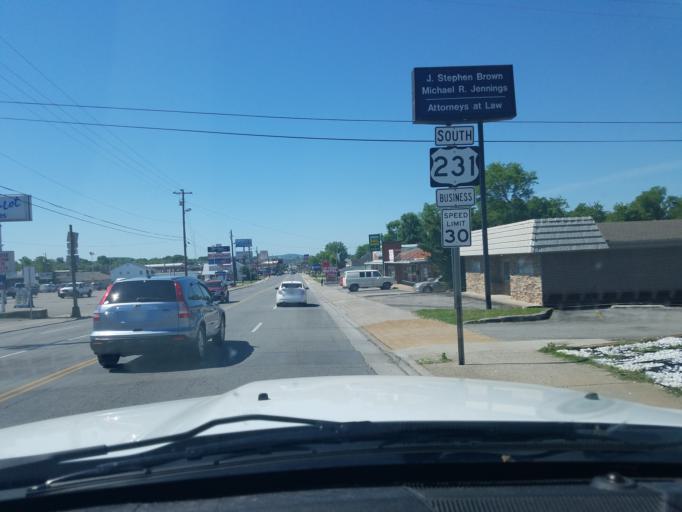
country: US
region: Tennessee
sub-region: Wilson County
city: Lebanon
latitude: 36.2122
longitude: -86.2905
